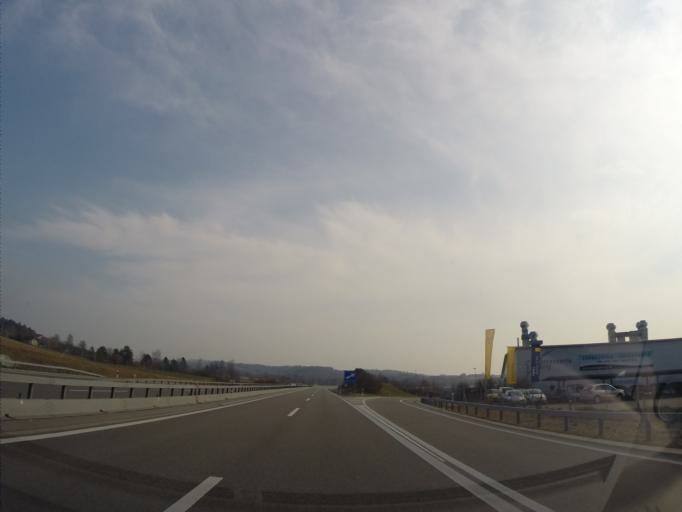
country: CH
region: Zurich
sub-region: Bezirk Andelfingen
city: Kleinandelfingen
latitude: 47.6050
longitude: 8.6882
